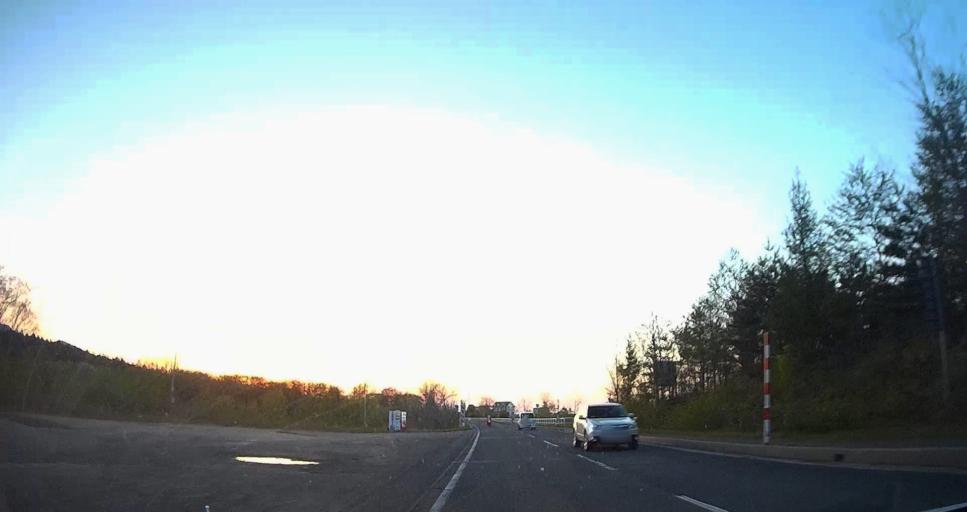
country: JP
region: Aomori
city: Misawa
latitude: 40.8667
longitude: 141.1094
